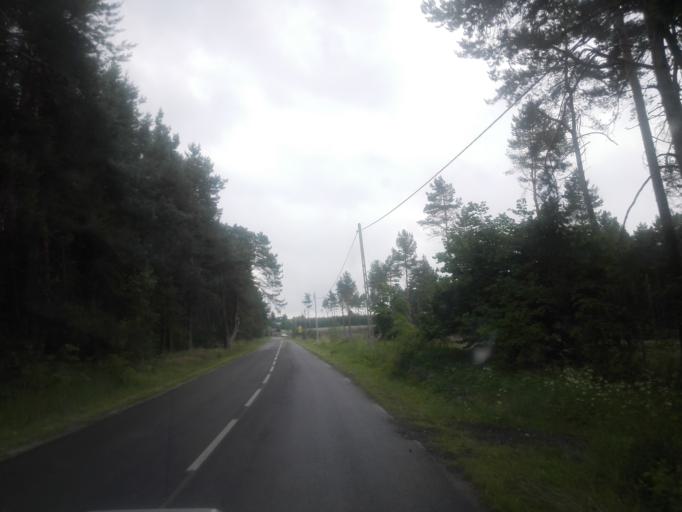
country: PL
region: Silesian Voivodeship
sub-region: Powiat myszkowski
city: Choron
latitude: 50.7094
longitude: 19.3385
